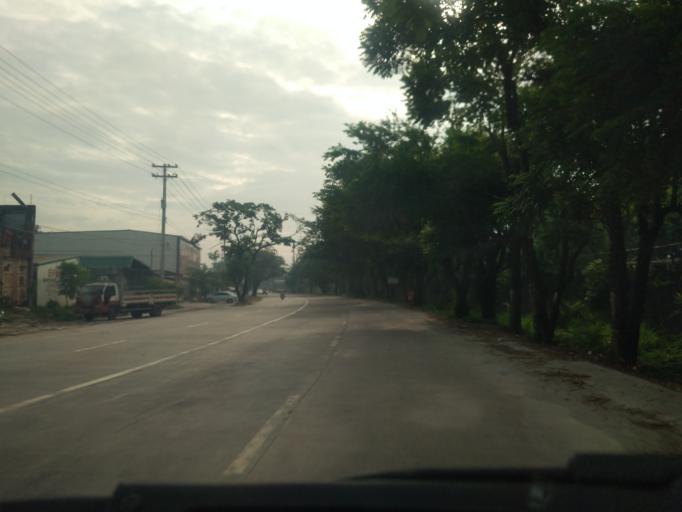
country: PH
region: Central Luzon
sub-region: Province of Pampanga
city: Calibutbut
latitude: 15.1270
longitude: 120.5787
